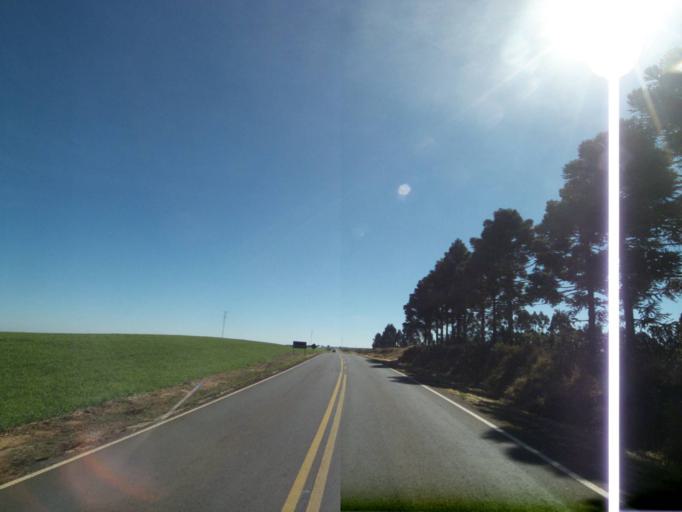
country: BR
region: Parana
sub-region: Castro
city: Castro
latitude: -24.6719
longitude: -50.2142
